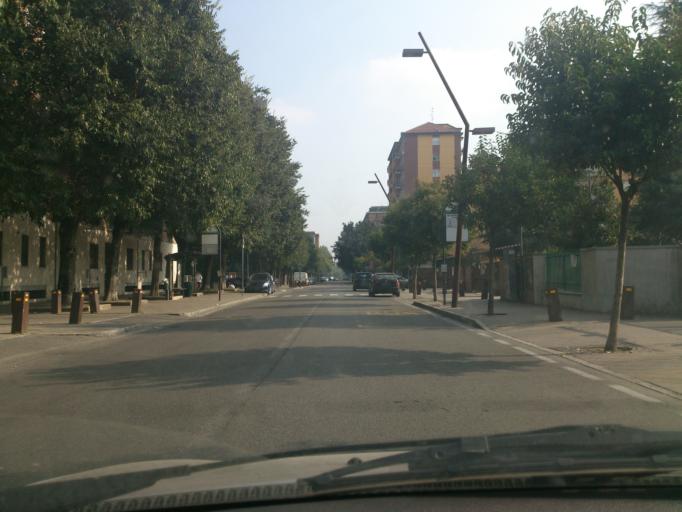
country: IT
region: Lombardy
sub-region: Citta metropolitana di Milano
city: Civesio
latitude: 45.4043
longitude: 9.2681
